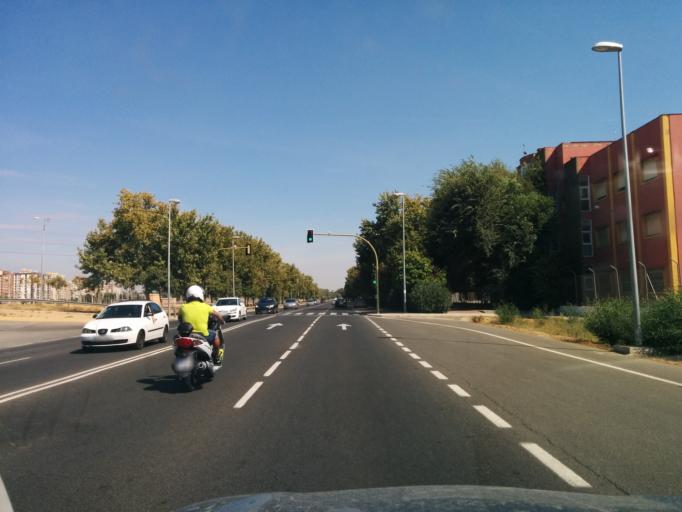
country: ES
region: Andalusia
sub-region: Provincia de Sevilla
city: San Juan de Aznalfarache
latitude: 37.3698
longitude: -6.0112
